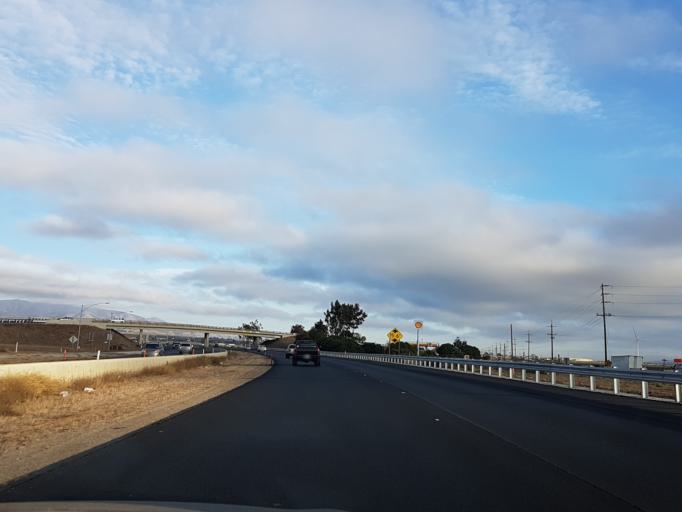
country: US
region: California
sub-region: Monterey County
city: Gonzales
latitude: 36.5246
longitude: -121.4668
